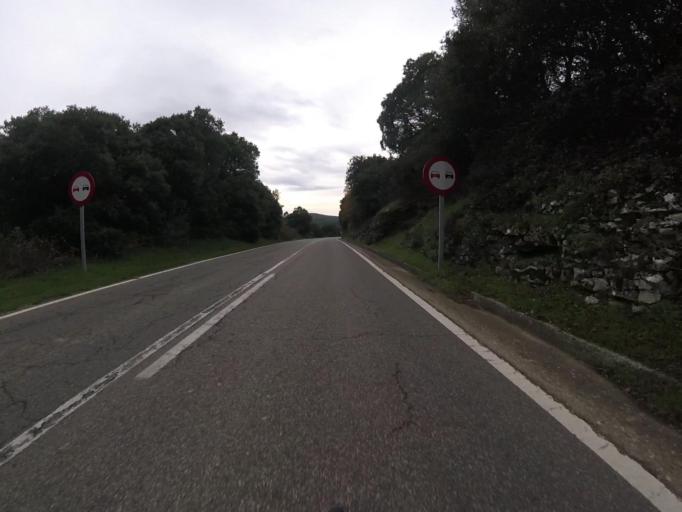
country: ES
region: Navarre
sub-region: Provincia de Navarra
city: Lezaun
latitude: 42.7436
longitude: -2.0207
